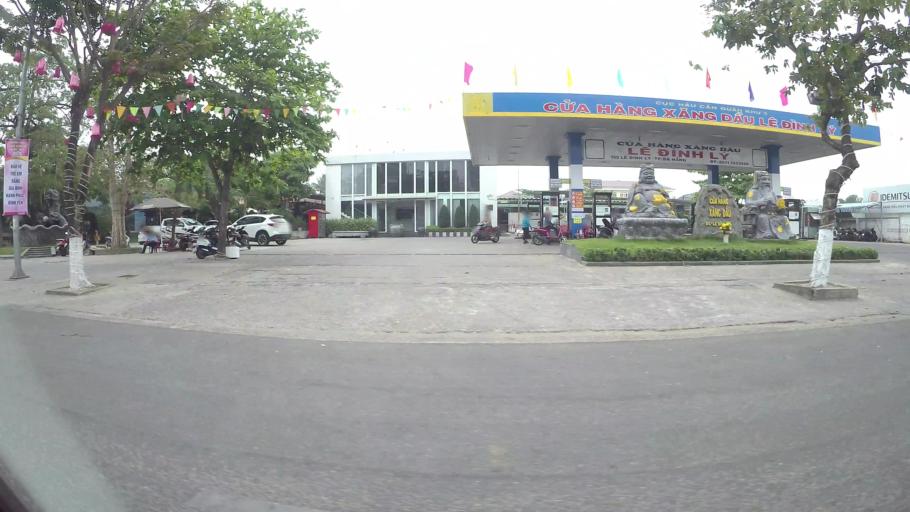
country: VN
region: Da Nang
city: Da Nang
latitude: 16.0534
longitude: 108.2112
